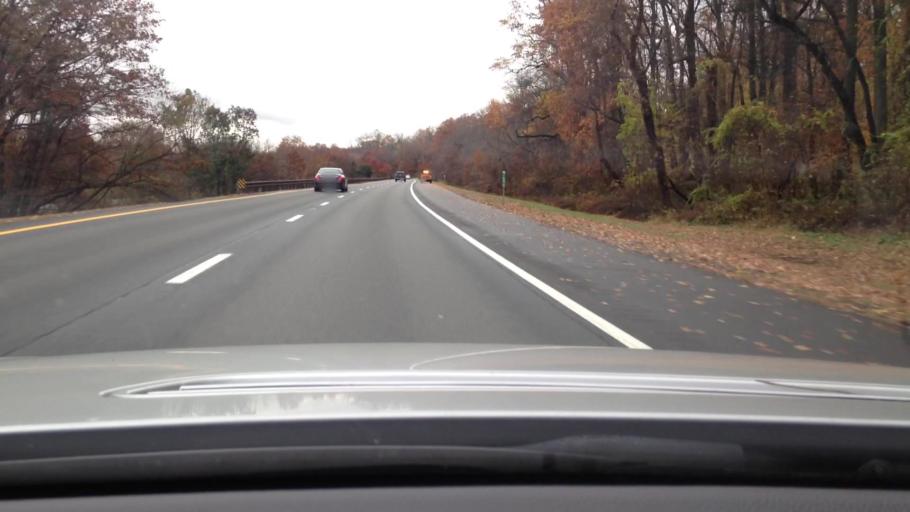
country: US
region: New Jersey
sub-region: Bergen County
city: Woodcliff Lake
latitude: 41.0288
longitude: -74.0695
